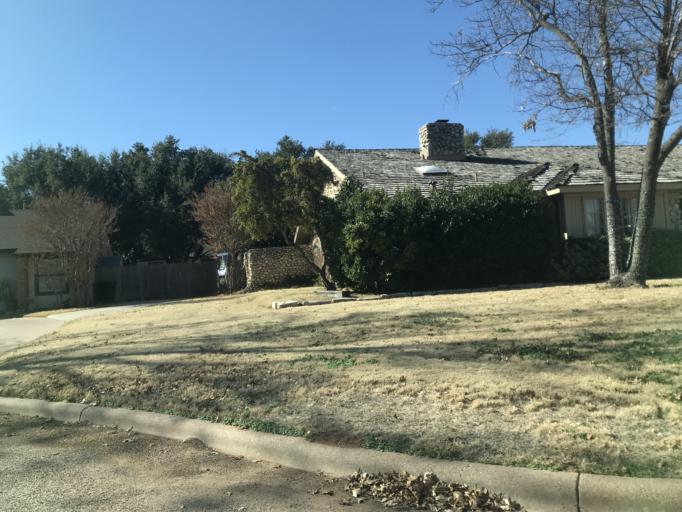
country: US
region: Texas
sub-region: Taylor County
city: Abilene
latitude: 32.3820
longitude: -99.7587
